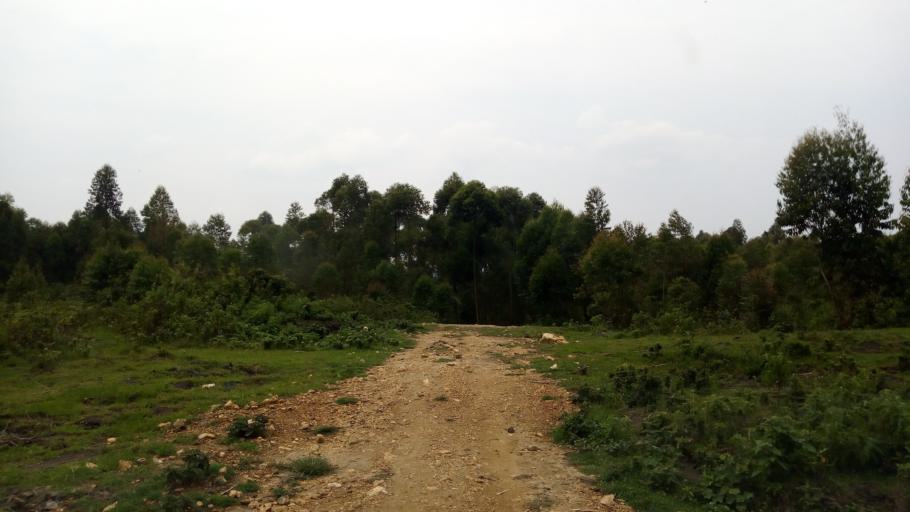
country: UG
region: Western Region
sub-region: Kisoro District
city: Kisoro
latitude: -1.2648
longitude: 29.6028
